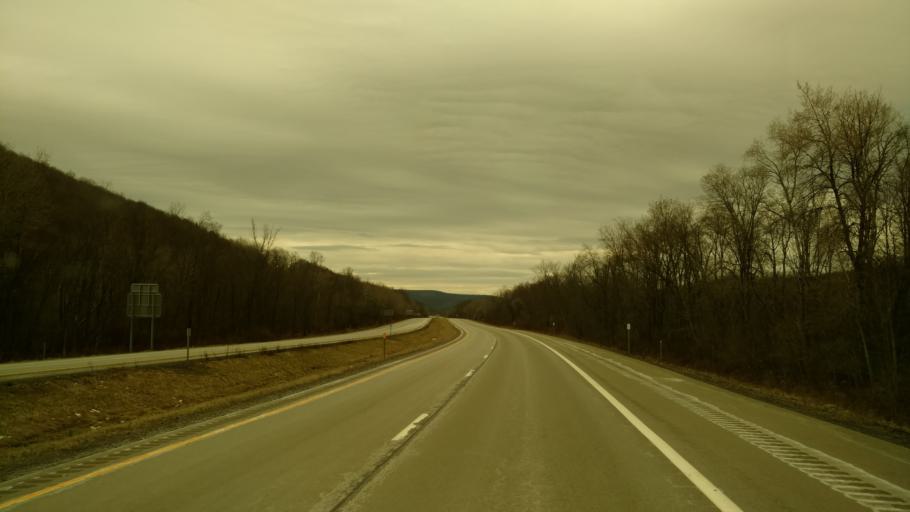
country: US
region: New York
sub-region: Cattaraugus County
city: Salamanca
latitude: 42.1489
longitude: -78.7655
